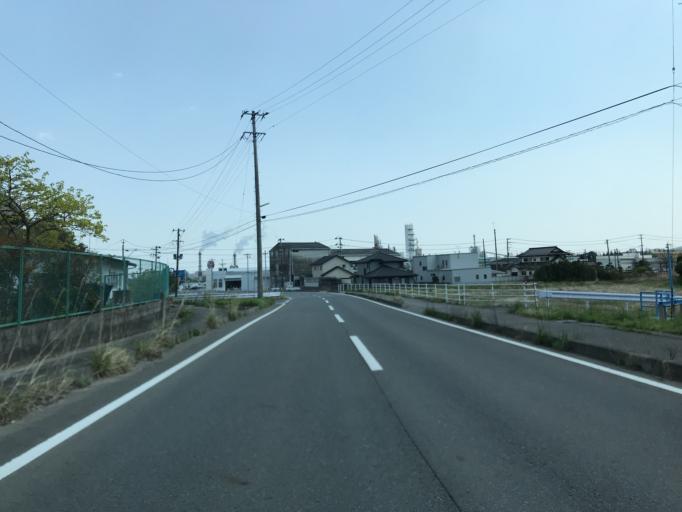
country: JP
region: Ibaraki
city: Kitaibaraki
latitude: 36.9109
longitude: 140.7711
